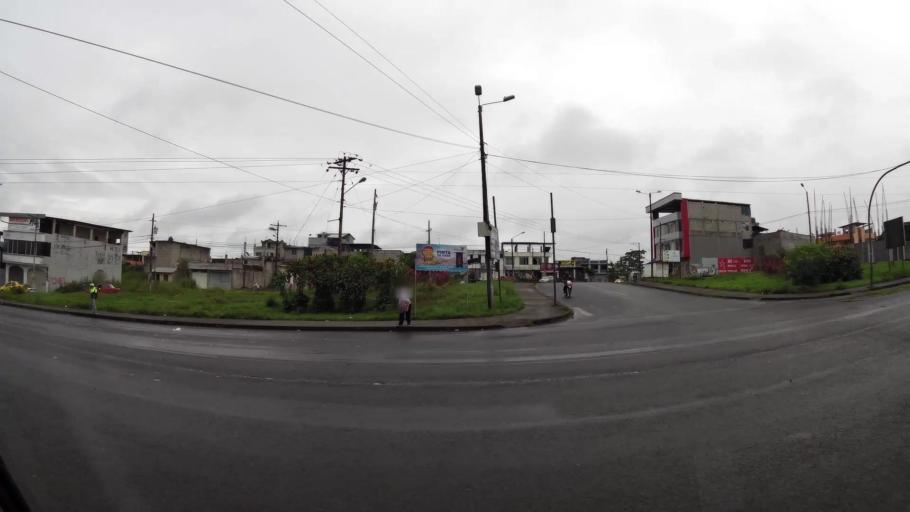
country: EC
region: Santo Domingo de los Tsachilas
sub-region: Canton Santo Domingo de los Colorados
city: Santo Domingo de los Colorados
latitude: -0.2380
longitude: -79.1819
